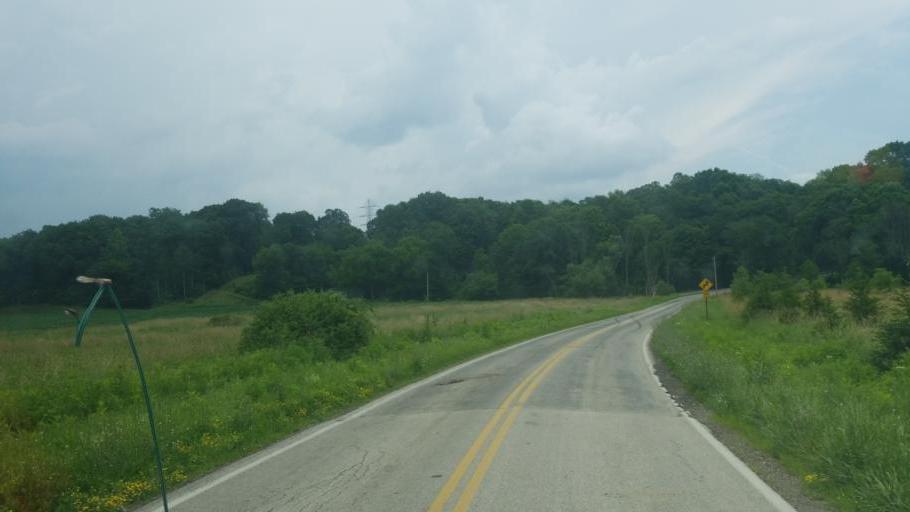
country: US
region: Ohio
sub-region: Wayne County
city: Wooster
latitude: 40.8660
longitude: -82.0078
